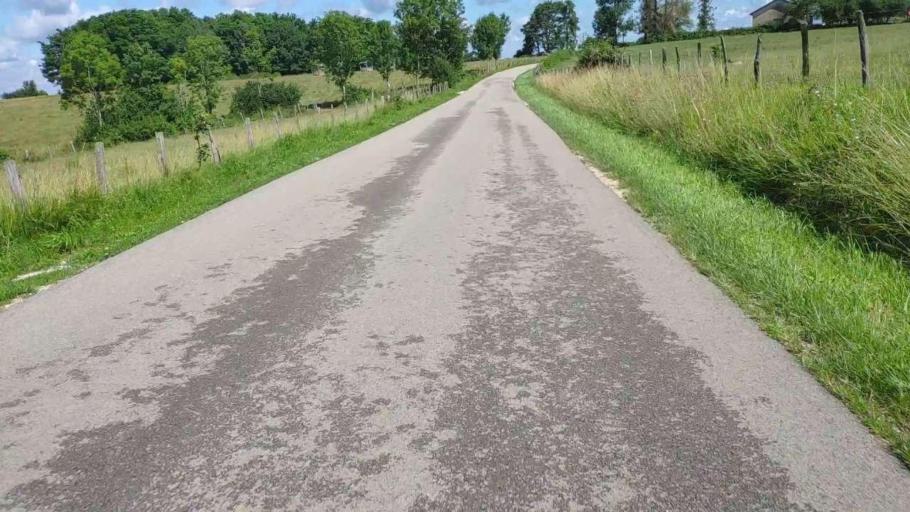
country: FR
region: Franche-Comte
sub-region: Departement du Jura
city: Bletterans
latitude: 46.8208
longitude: 5.5589
